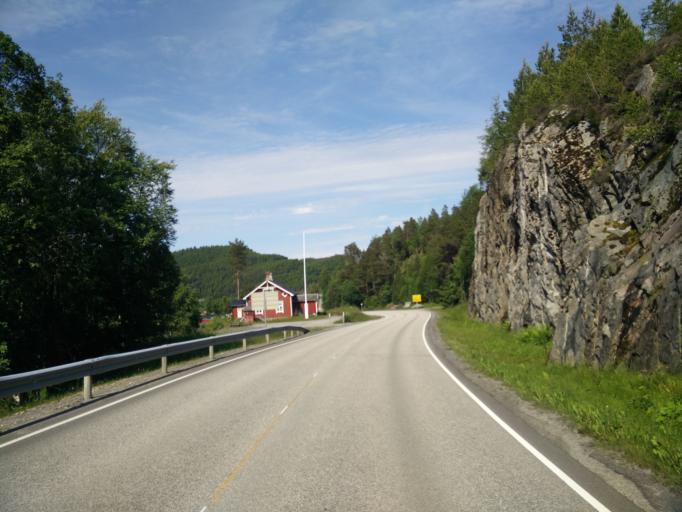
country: NO
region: More og Romsdal
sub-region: Kristiansund
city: Rensvik
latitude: 63.0130
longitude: 8.0016
